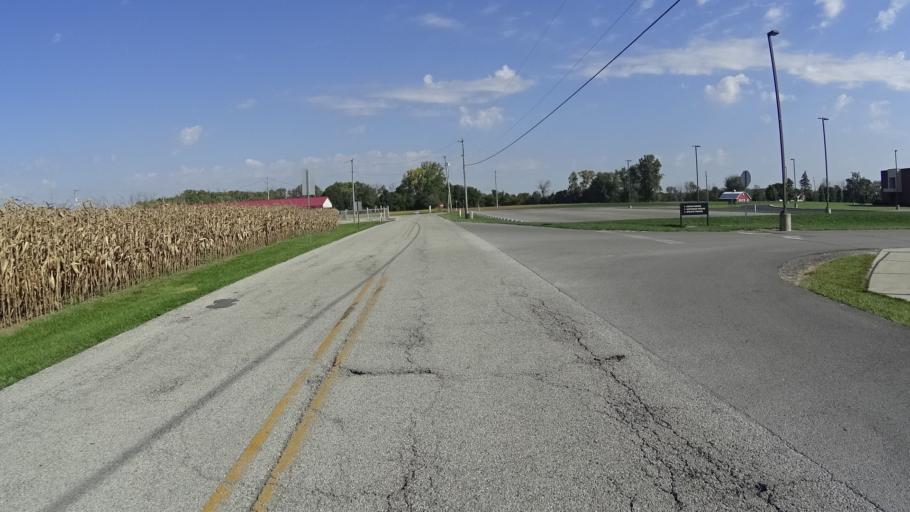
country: US
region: Indiana
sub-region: Madison County
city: Lapel
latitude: 40.0765
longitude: -85.8434
